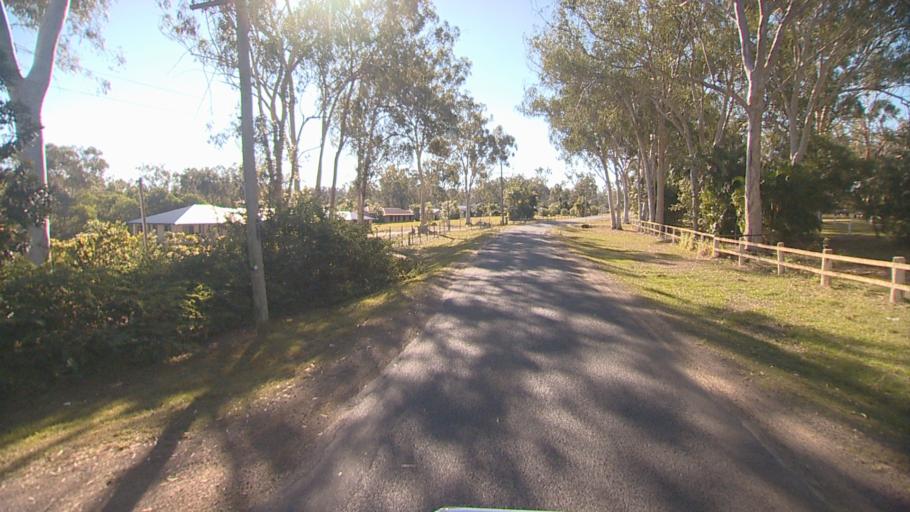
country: AU
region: Queensland
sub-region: Logan
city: Chambers Flat
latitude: -27.7341
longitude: 153.0779
